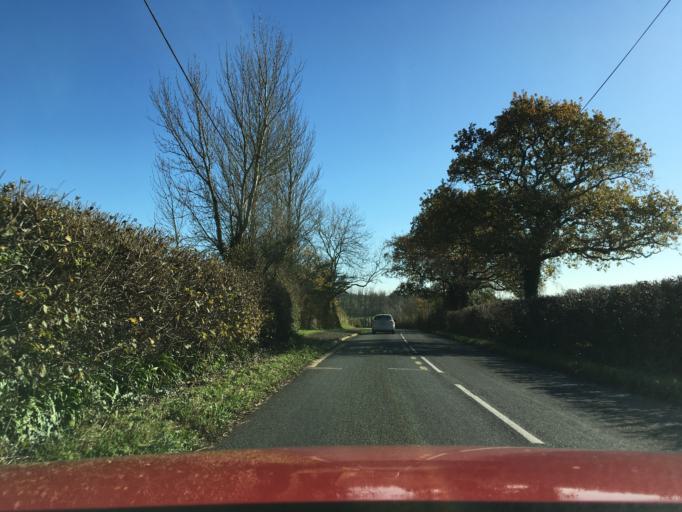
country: GB
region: England
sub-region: Somerset
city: Yeovil
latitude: 50.9606
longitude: -2.6618
